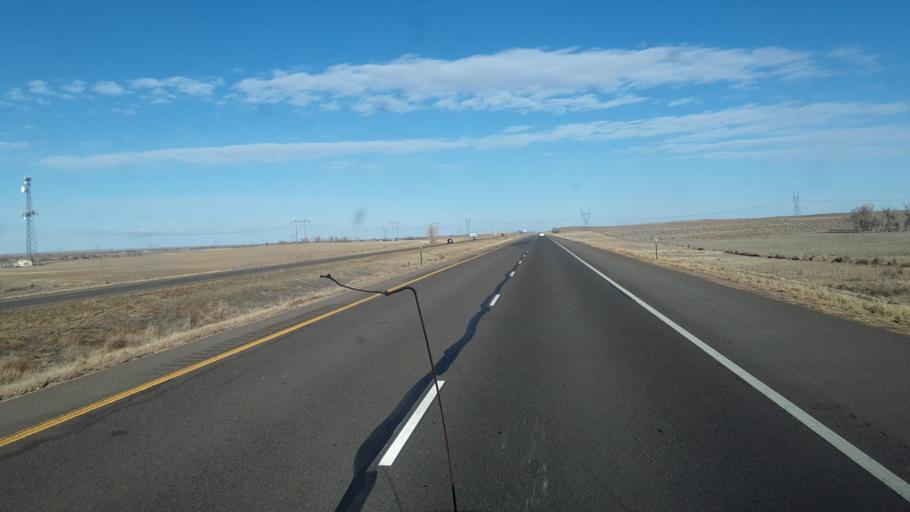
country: US
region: Colorado
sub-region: Morgan County
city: Brush
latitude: 40.2844
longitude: -103.5562
